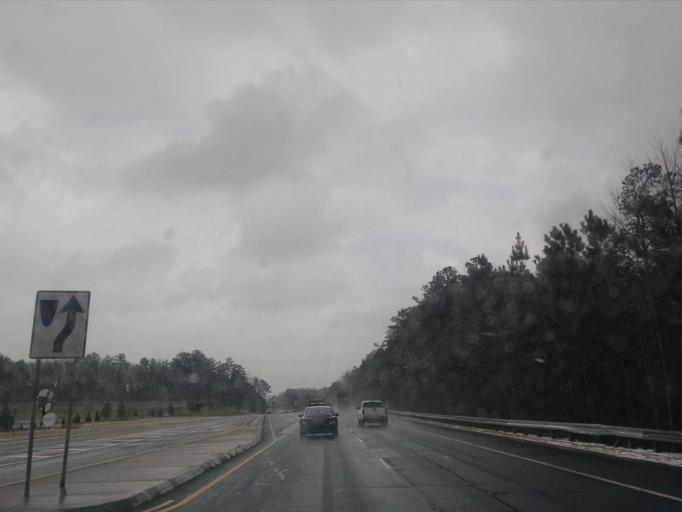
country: US
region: Georgia
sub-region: Gwinnett County
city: Sugar Hill
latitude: 34.0821
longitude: -84.0543
